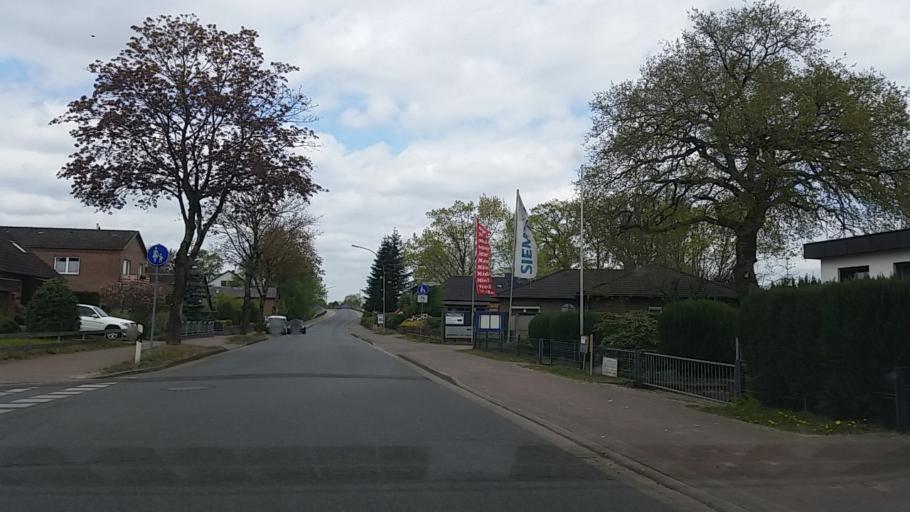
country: DE
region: Lower Saxony
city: Tostedt
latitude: 53.2717
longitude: 9.7381
